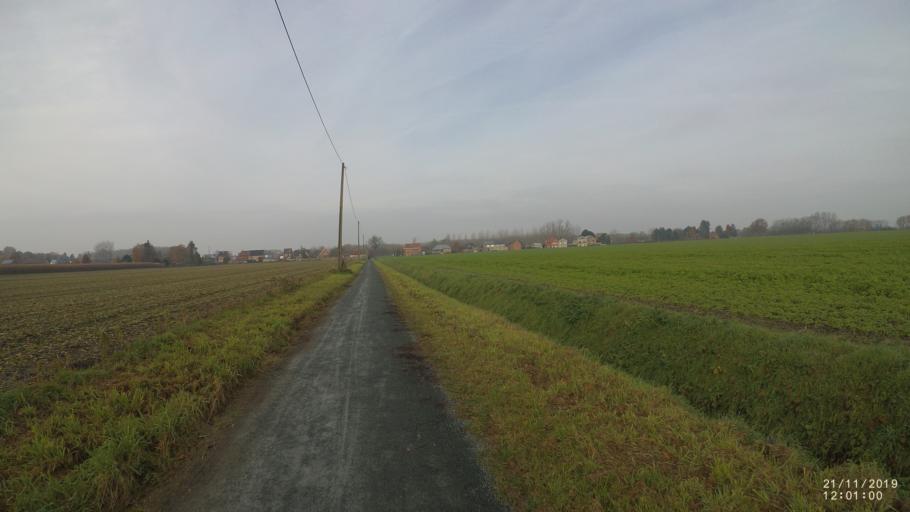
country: BE
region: Flanders
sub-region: Provincie Limburg
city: Sint-Truiden
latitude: 50.8282
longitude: 5.2193
